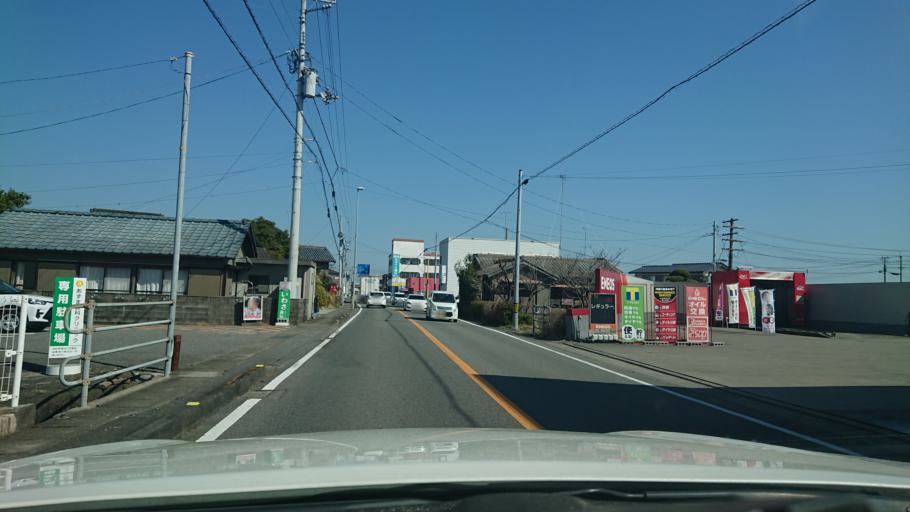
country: JP
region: Tokushima
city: Anan
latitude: 33.9480
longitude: 134.6261
